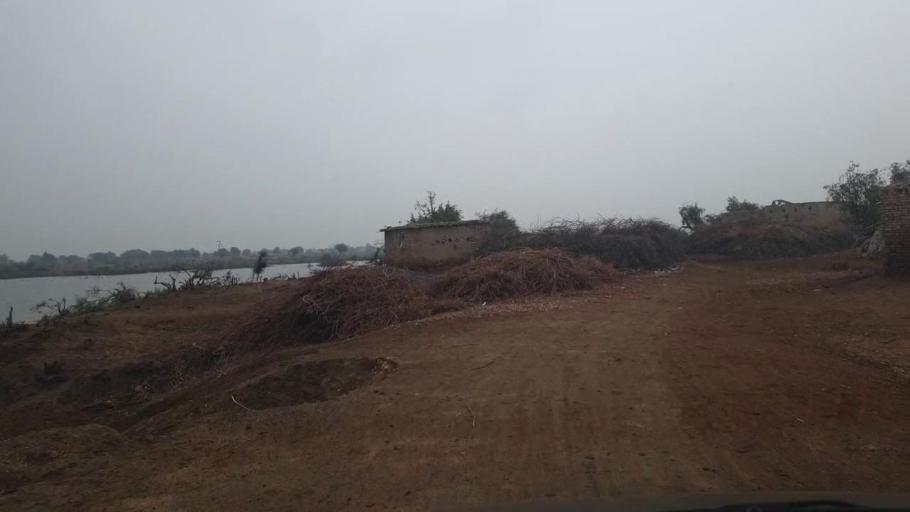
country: PK
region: Sindh
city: Tando Adam
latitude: 25.8362
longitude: 68.6955
